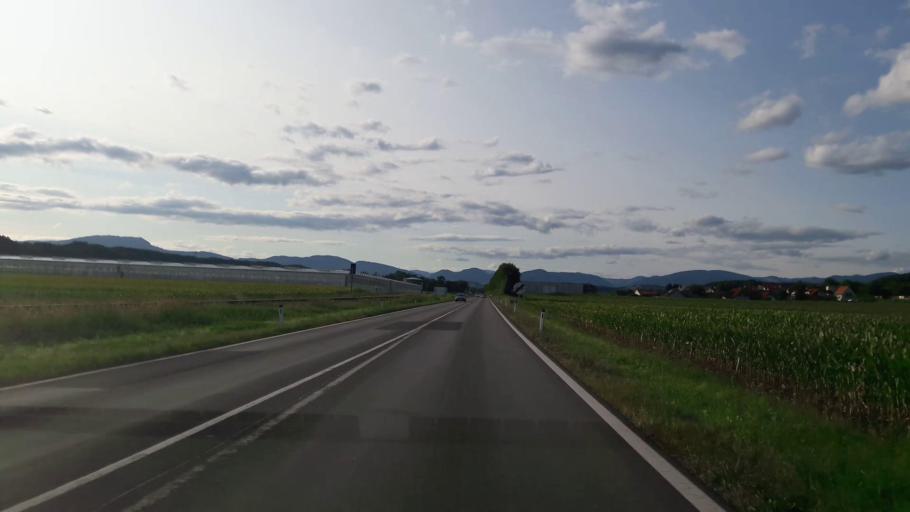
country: AT
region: Styria
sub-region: Politischer Bezirk Weiz
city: Gleisdorf
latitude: 47.1279
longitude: 15.6901
